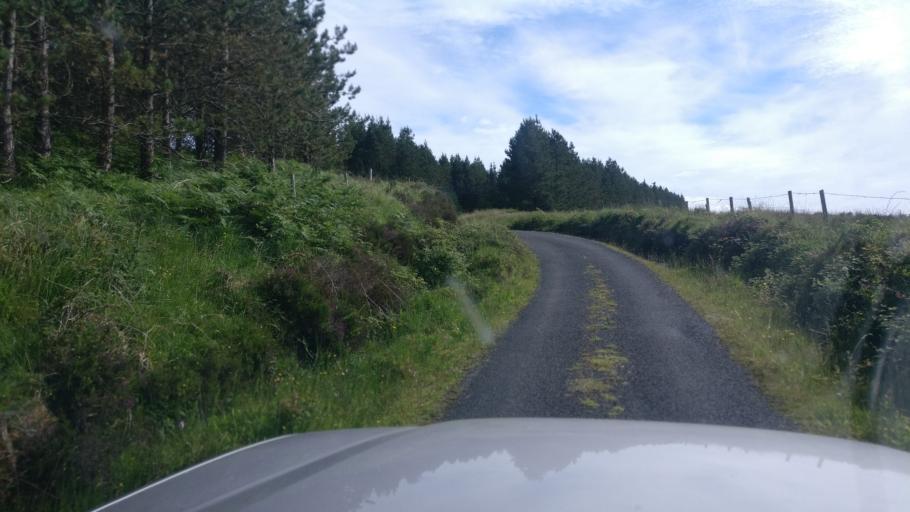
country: IE
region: Connaught
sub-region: County Galway
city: Gort
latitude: 53.0889
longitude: -8.6953
